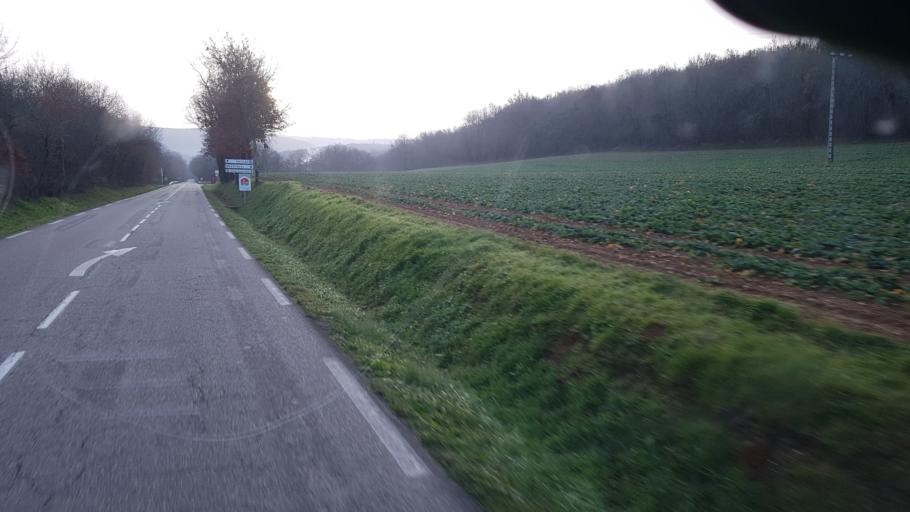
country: FR
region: Midi-Pyrenees
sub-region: Departement du Tarn-et-Garonne
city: Montricoux
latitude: 44.0718
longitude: 1.6475
